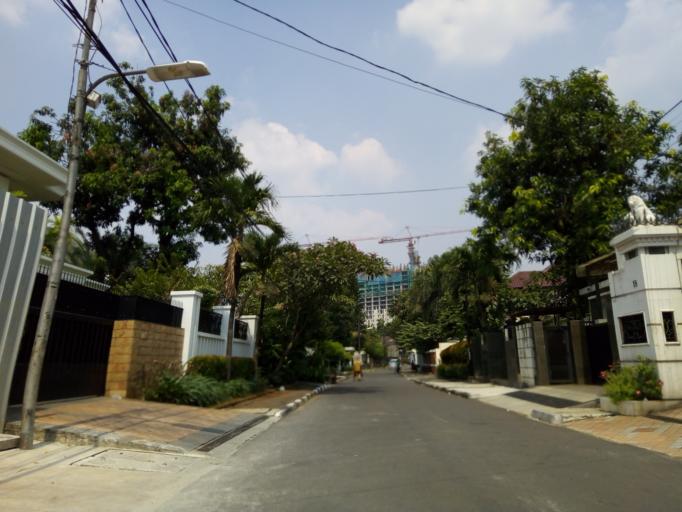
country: ID
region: Jakarta Raya
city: Jakarta
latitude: -6.2043
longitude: 106.8402
